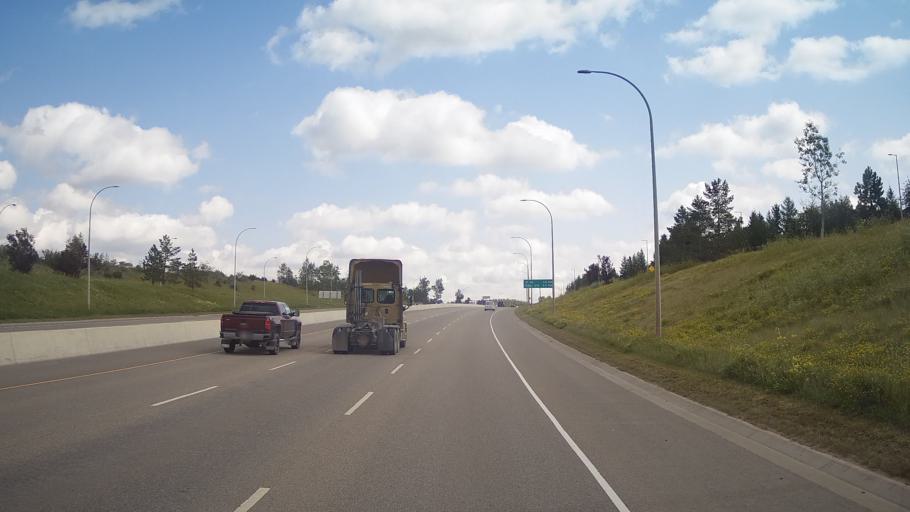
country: CA
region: Alberta
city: Sherwood Park
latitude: 53.4870
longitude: -113.3931
